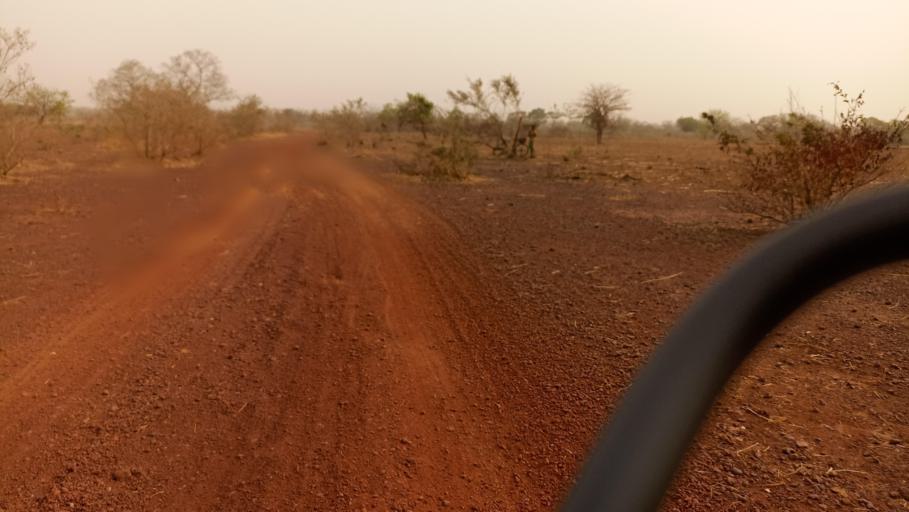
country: BF
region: Nord
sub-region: Province du Zondoma
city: Gourcy
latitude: 13.1521
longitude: -2.5955
